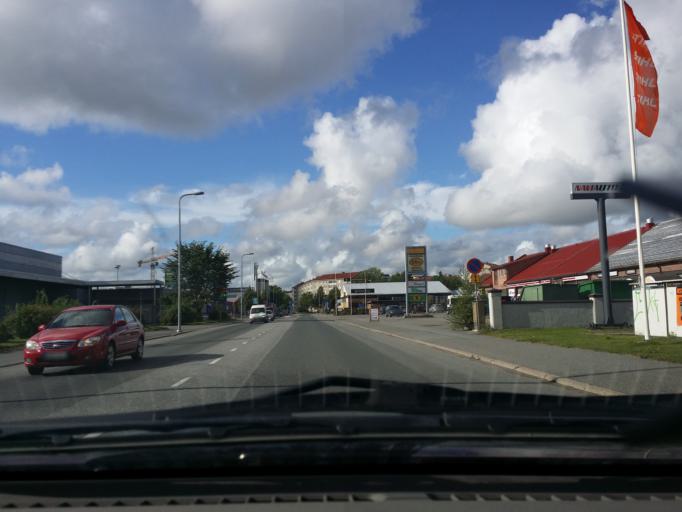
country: FI
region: Satakunta
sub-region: Pori
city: Pori
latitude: 61.4750
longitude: 21.7964
